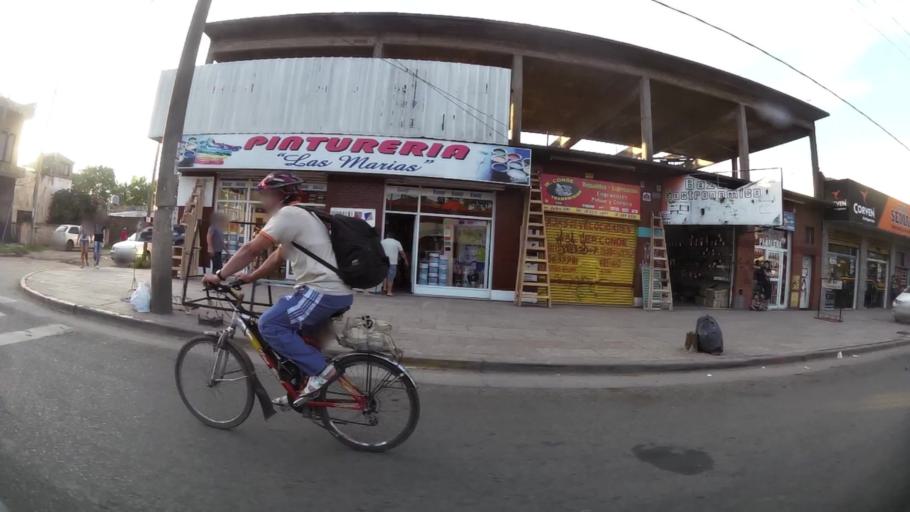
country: AR
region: Buenos Aires
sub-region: Partido de Merlo
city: Merlo
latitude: -34.6798
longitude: -58.7587
